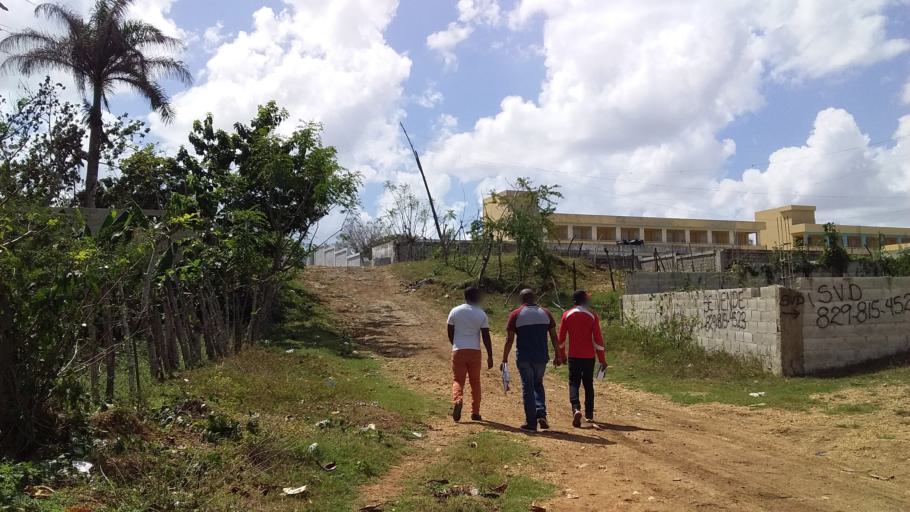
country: DO
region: Santo Domingo
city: Guerra
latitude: 18.5645
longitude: -69.7813
